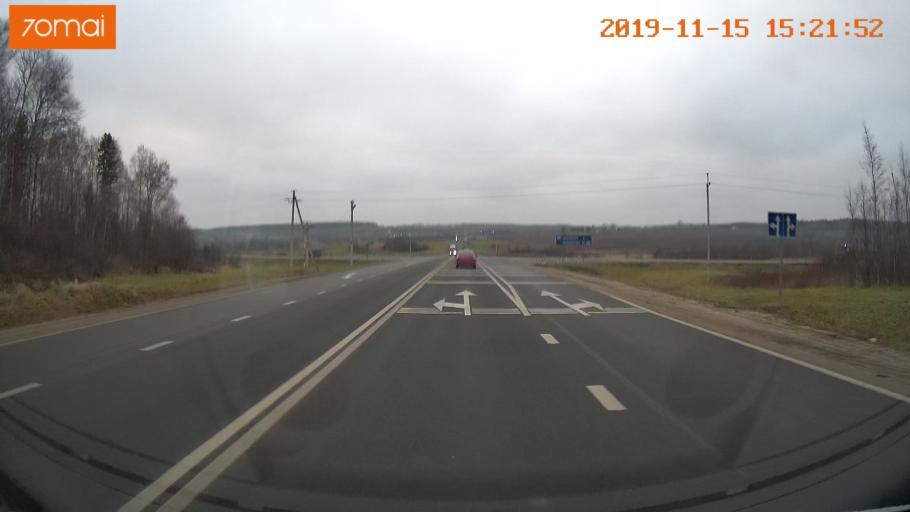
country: RU
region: Jaroslavl
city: Danilov
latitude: 58.2086
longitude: 40.1397
